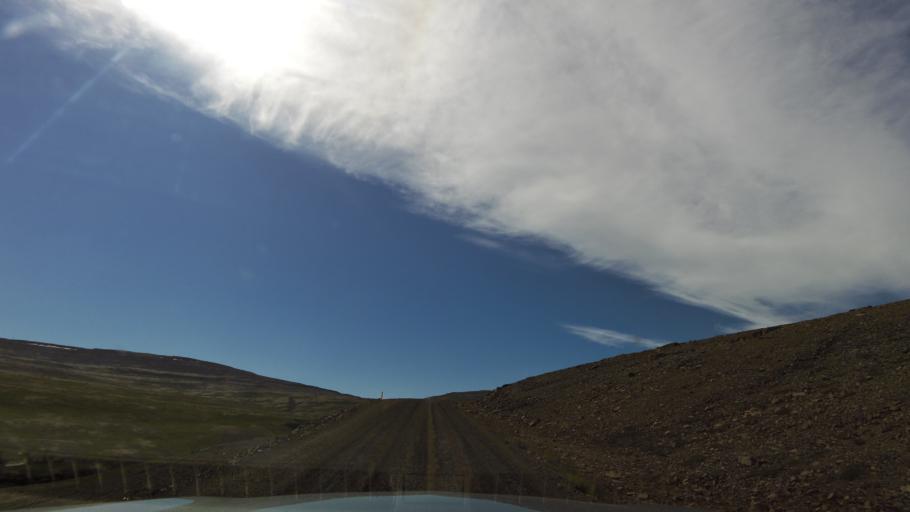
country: IS
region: West
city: Olafsvik
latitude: 65.5194
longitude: -23.9300
